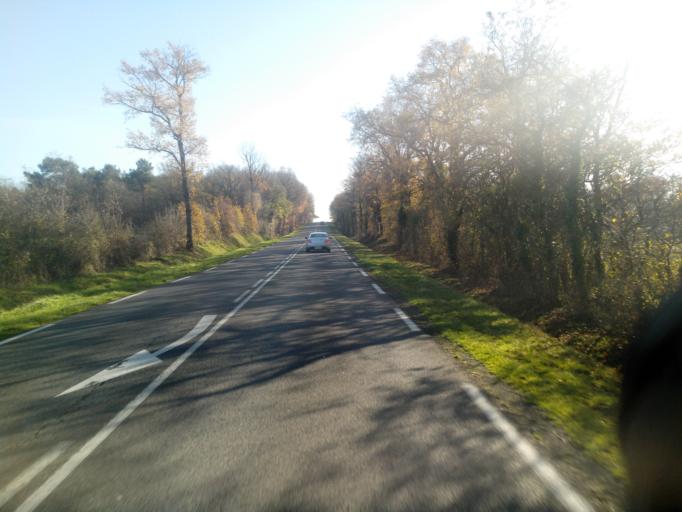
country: FR
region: Poitou-Charentes
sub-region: Departement de la Vienne
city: Lussac-les-Chateaux
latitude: 46.3568
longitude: 0.7802
